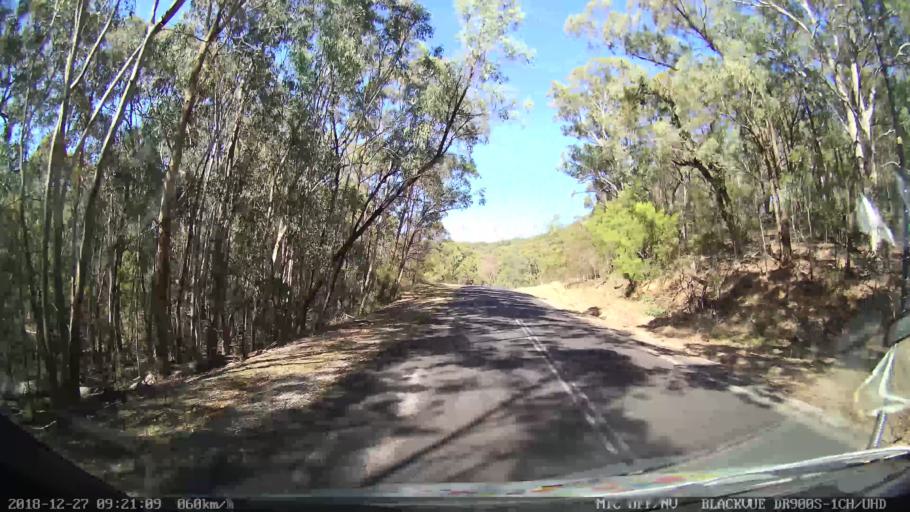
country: AU
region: New South Wales
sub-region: Lithgow
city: Portland
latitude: -33.1221
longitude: 150.0189
